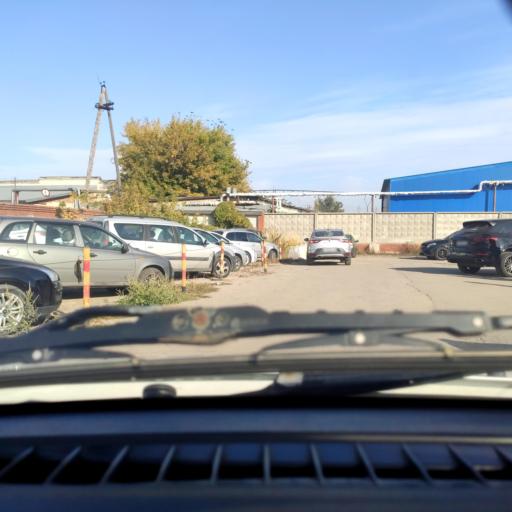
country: RU
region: Samara
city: Tol'yatti
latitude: 53.5468
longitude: 49.4330
